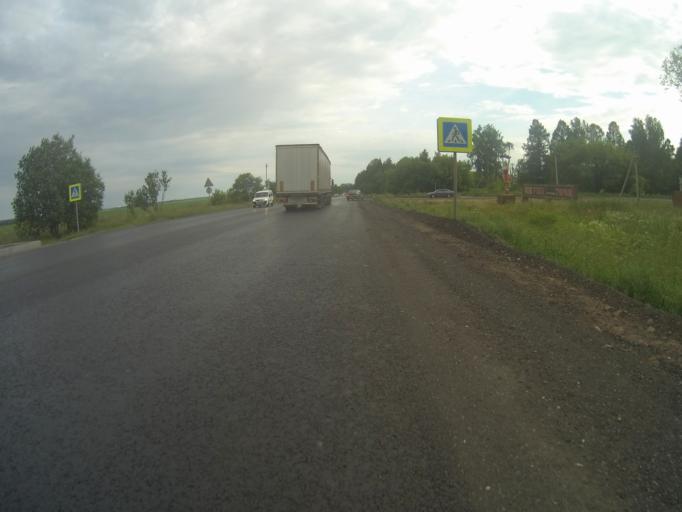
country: RU
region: Vladimir
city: Bogolyubovo
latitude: 56.2214
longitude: 40.4417
